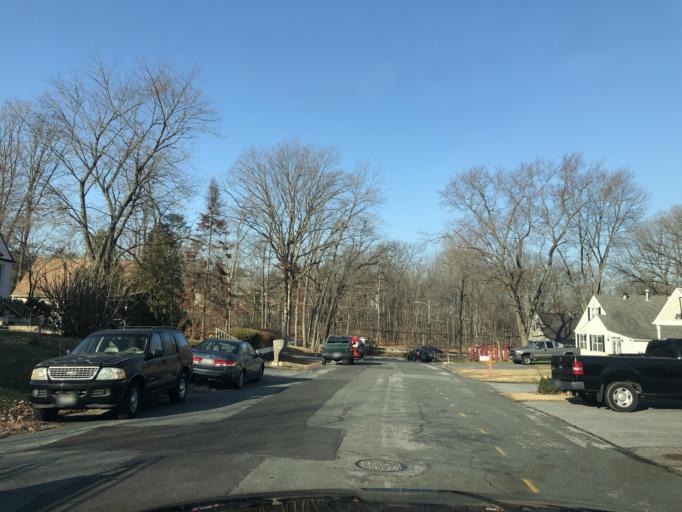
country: US
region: Maryland
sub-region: Anne Arundel County
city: Odenton
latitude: 39.0799
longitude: -76.7007
